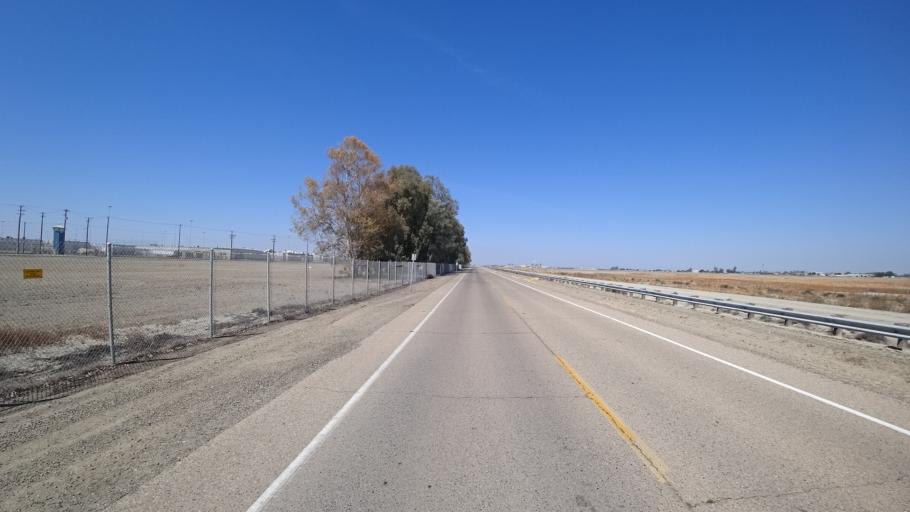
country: US
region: California
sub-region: Kings County
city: Corcoran
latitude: 36.0650
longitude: -119.5479
